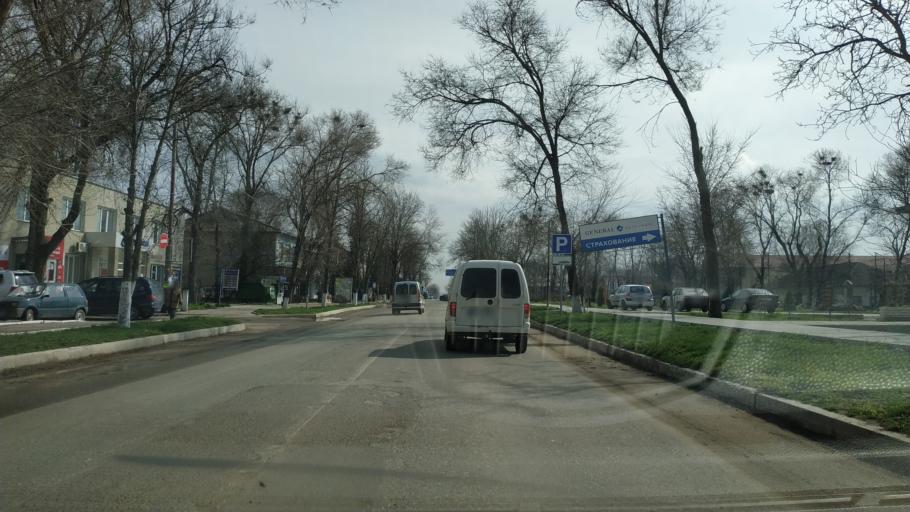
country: MD
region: Gagauzia
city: Vulcanesti
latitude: 45.6853
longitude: 28.4052
